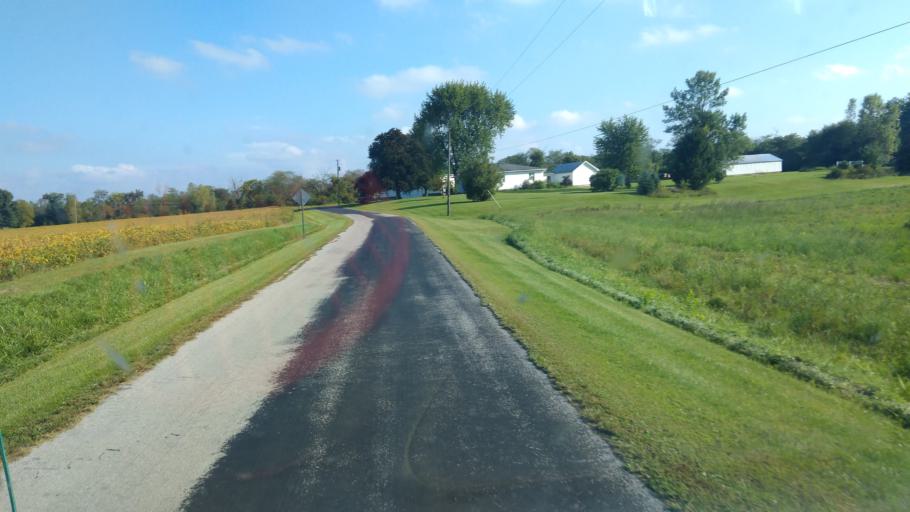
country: US
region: Ohio
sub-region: Hardin County
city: Forest
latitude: 40.7197
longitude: -83.4592
